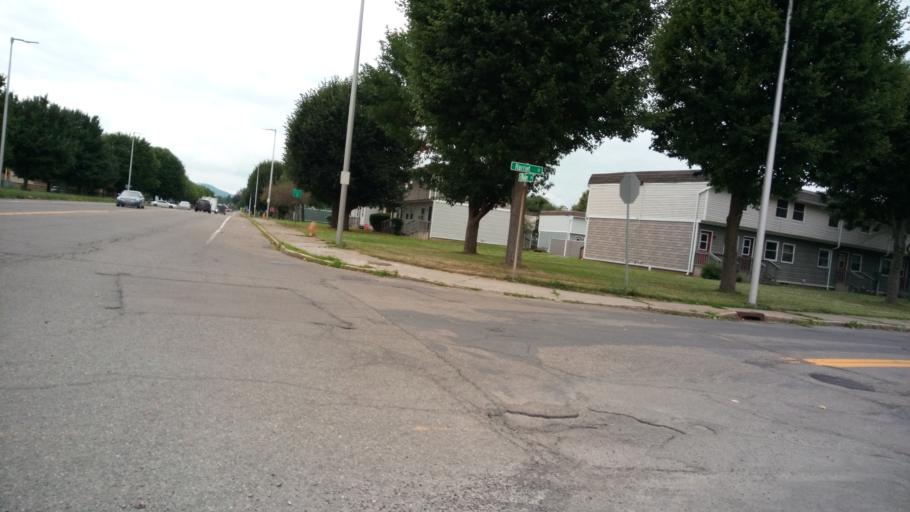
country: US
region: New York
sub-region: Chemung County
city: Elmira
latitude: 42.0898
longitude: -76.7898
